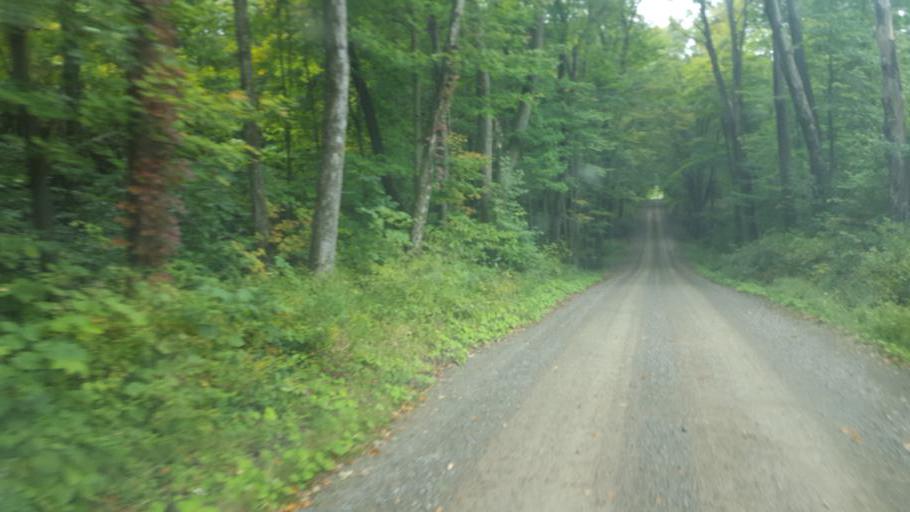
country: US
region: Pennsylvania
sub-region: Crawford County
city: Pymatuning Central
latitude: 41.5254
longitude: -80.3967
